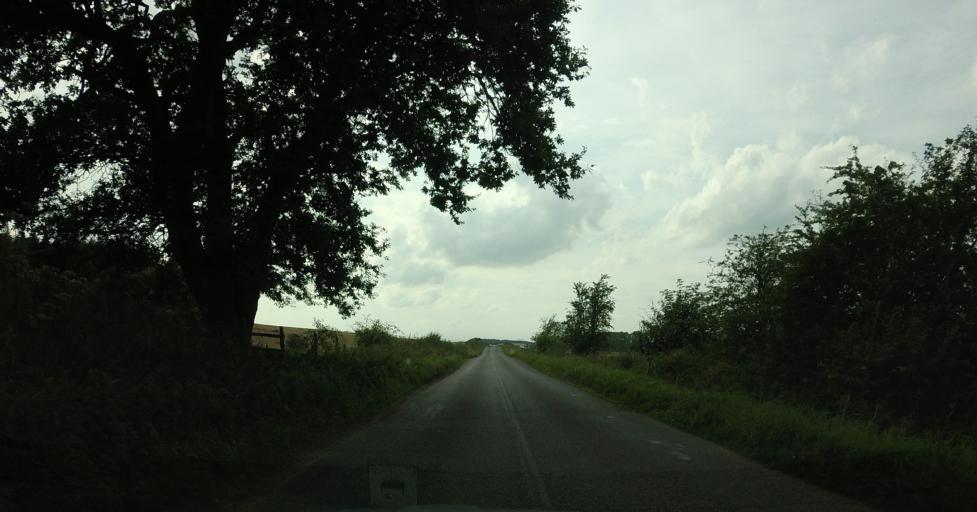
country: GB
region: Scotland
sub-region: Perth and Kinross
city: Methven
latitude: 56.3871
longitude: -3.6178
